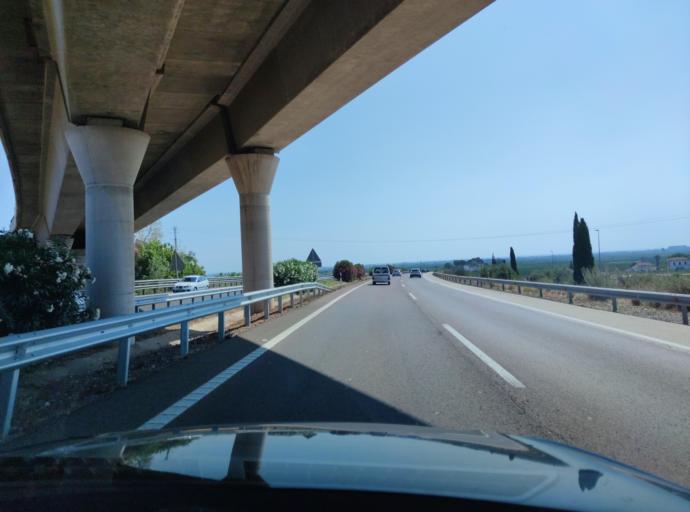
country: ES
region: Valencia
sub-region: Provincia de Valencia
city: Sagunto
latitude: 39.7014
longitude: -0.2648
